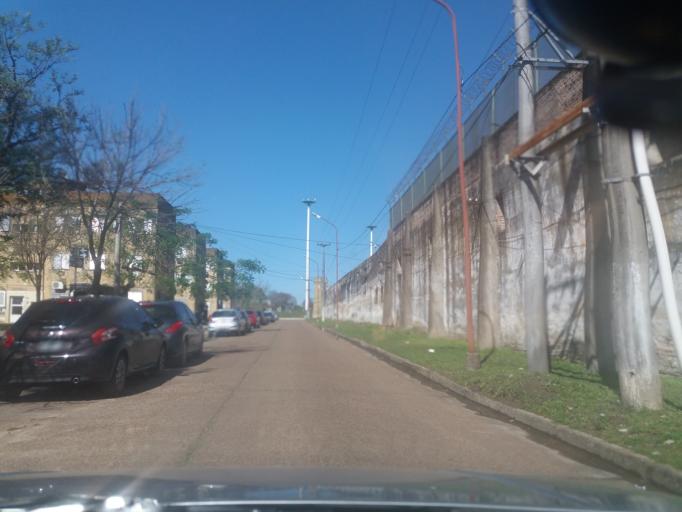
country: AR
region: Corrientes
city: Corrientes
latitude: -27.4725
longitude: -58.8499
